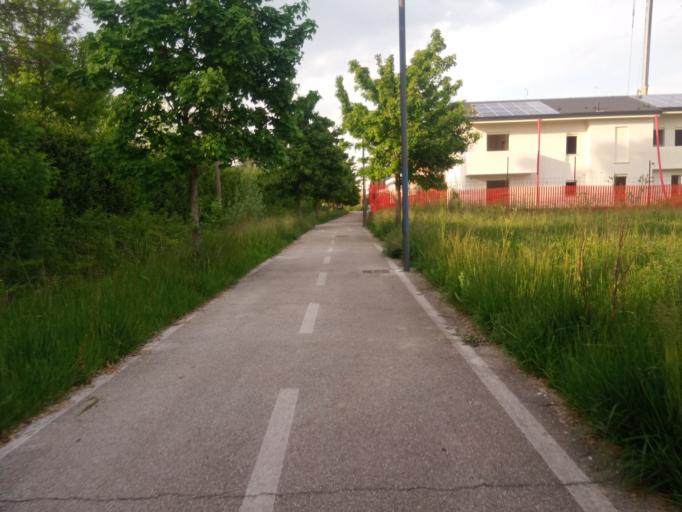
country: IT
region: Veneto
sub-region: Provincia di Padova
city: Mandriola-Sant'Agostino
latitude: 45.3797
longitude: 11.8465
